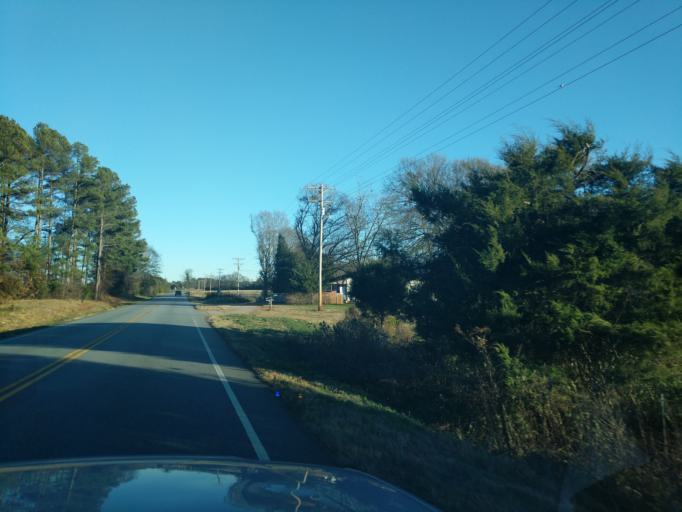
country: US
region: South Carolina
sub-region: Oconee County
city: Seneca
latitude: 34.5942
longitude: -82.9973
